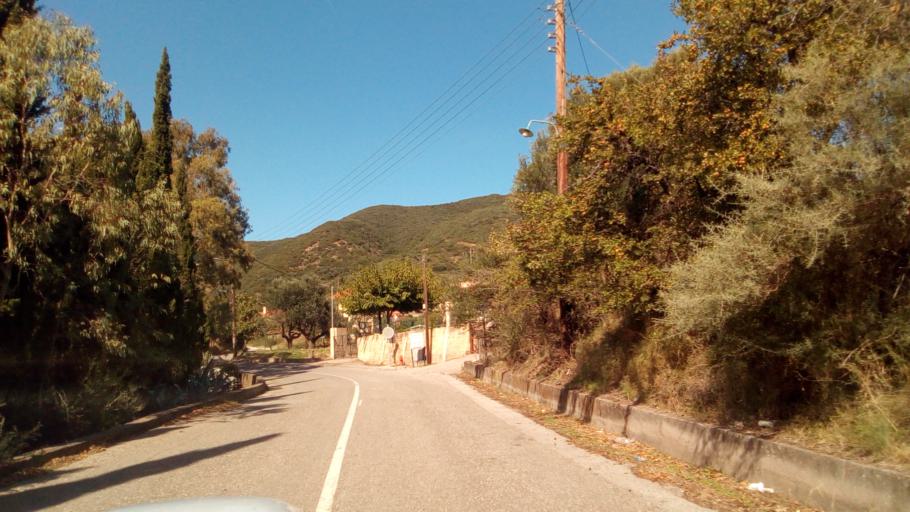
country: GR
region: West Greece
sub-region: Nomos Aitolias kai Akarnanias
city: Antirrio
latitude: 38.3577
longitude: 21.7539
